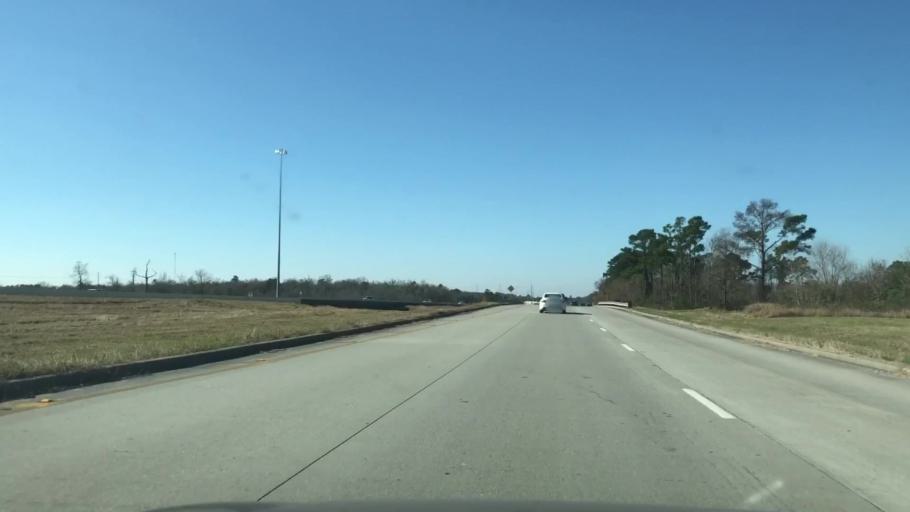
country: US
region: Texas
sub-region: Harris County
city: Cloverleaf
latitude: 29.8288
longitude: -95.1857
